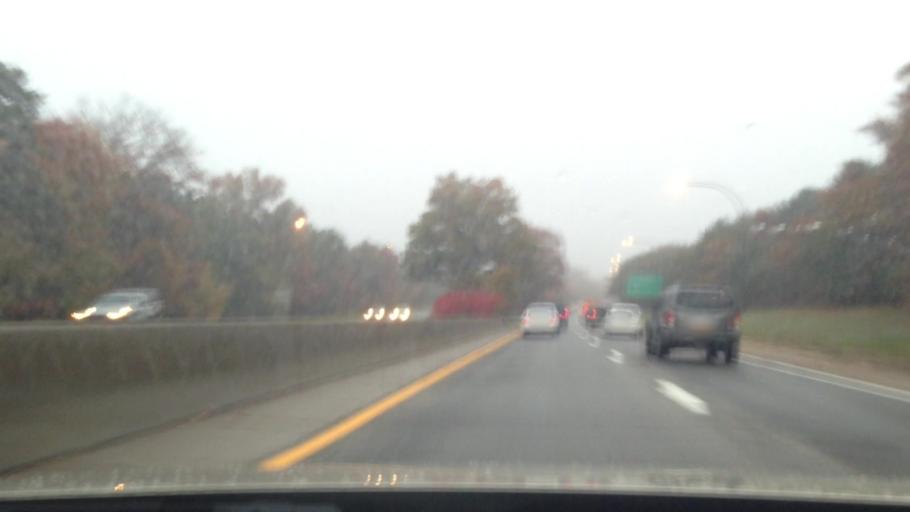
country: US
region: New York
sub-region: Suffolk County
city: Bay Wood
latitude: 40.7752
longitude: -73.2802
